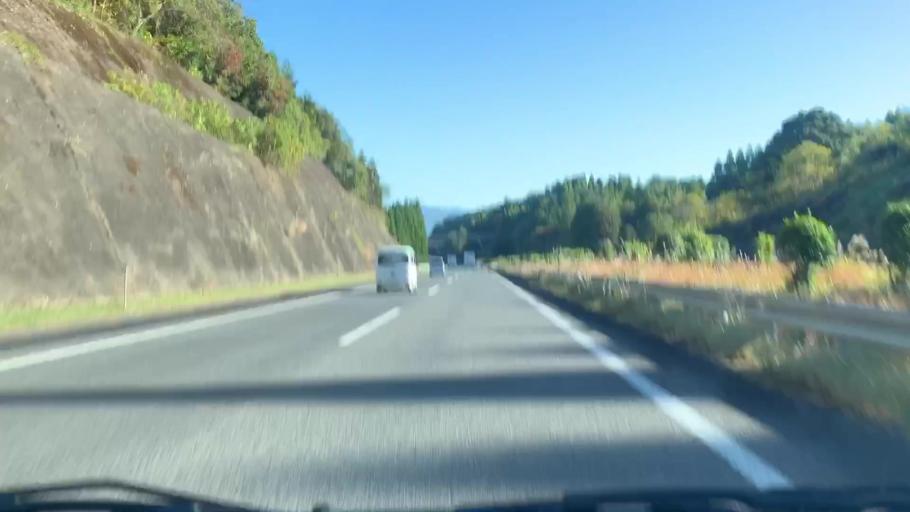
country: JP
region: Saga Prefecture
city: Takeocho-takeo
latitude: 33.2469
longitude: 130.0719
